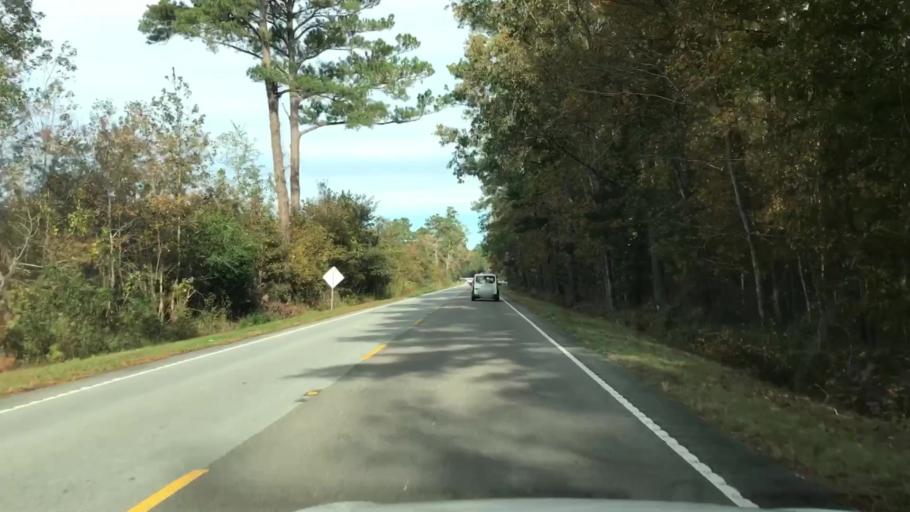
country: US
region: South Carolina
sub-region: Colleton County
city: Walterboro
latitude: 32.8446
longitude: -80.5909
